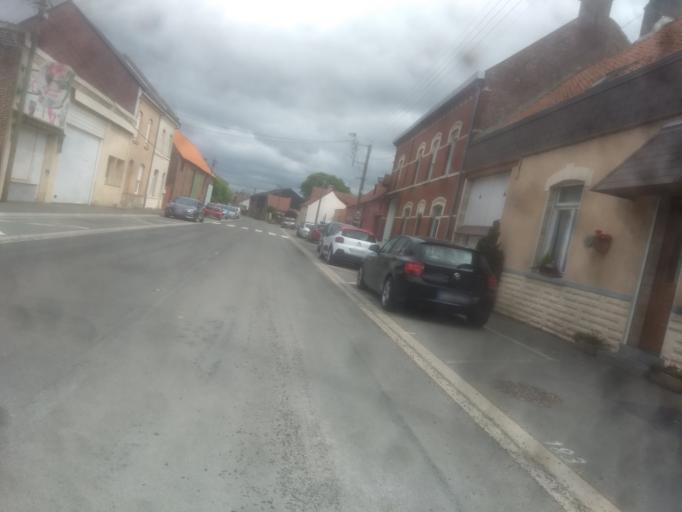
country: FR
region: Nord-Pas-de-Calais
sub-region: Departement du Pas-de-Calais
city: Thelus
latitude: 50.3554
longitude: 2.7943
